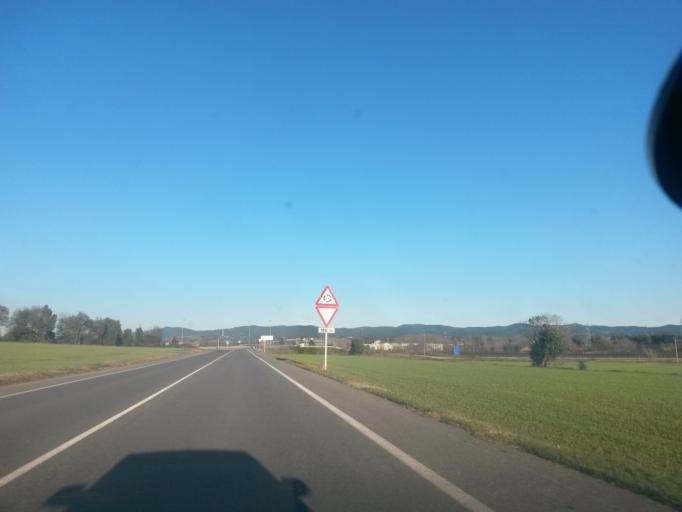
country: ES
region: Catalonia
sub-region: Provincia de Girona
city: Vilablareix
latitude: 41.9418
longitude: 2.7861
